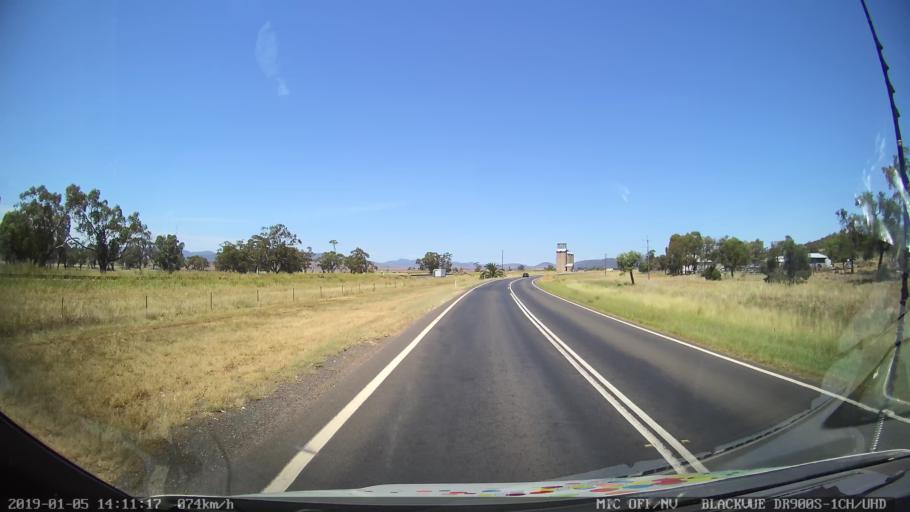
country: AU
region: New South Wales
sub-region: Gunnedah
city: Gunnedah
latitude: -31.2439
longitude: 150.4560
